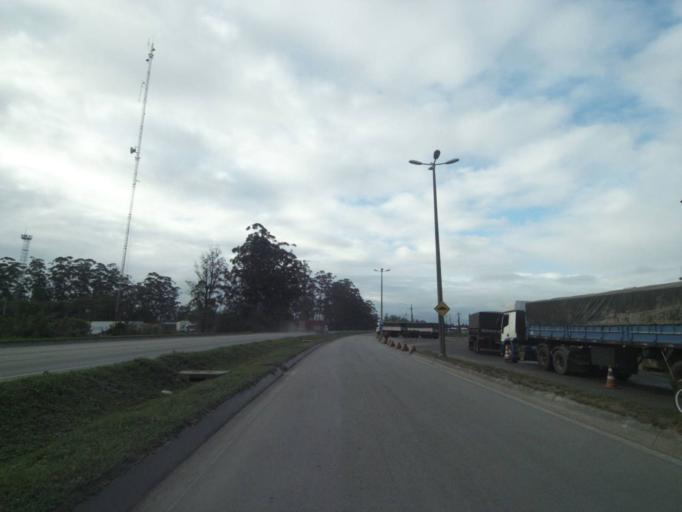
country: BR
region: Parana
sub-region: Paranagua
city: Paranagua
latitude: -25.5406
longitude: -48.5586
